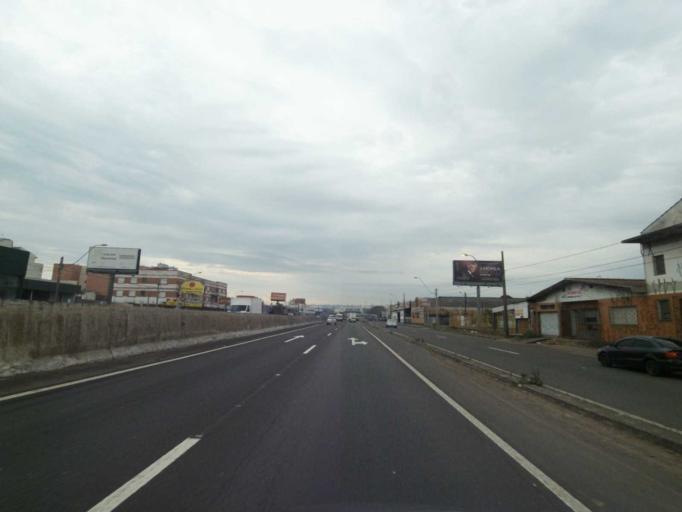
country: BR
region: Rio Grande do Sul
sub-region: Sao Leopoldo
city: Sao Leopoldo
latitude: -29.7665
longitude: -51.1539
